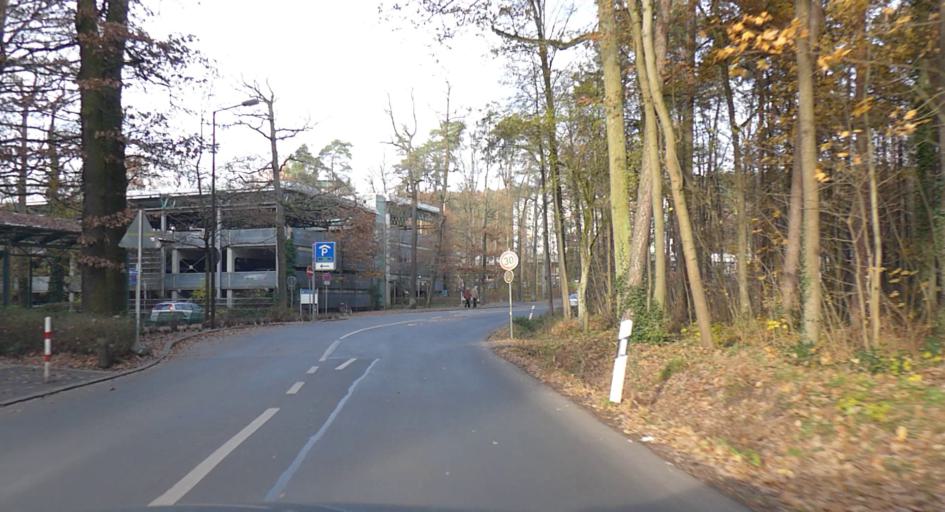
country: DE
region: Bavaria
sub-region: Regierungsbezirk Mittelfranken
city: Bubenreuth
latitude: 49.6102
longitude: 11.0203
